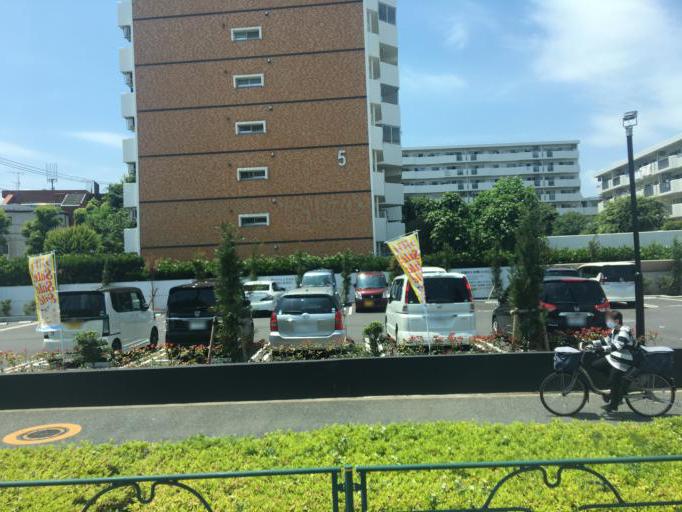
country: JP
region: Saitama
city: Shimotoda
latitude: 35.7640
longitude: 139.6841
